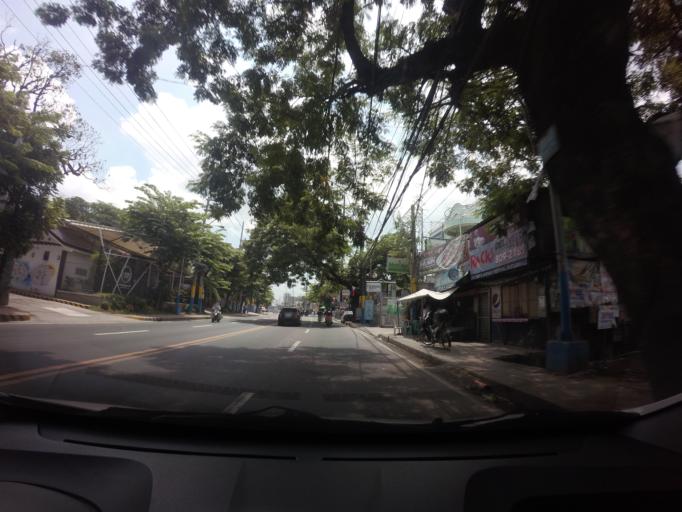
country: PH
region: Calabarzon
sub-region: Province of Laguna
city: San Pedro
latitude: 14.4020
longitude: 121.0472
